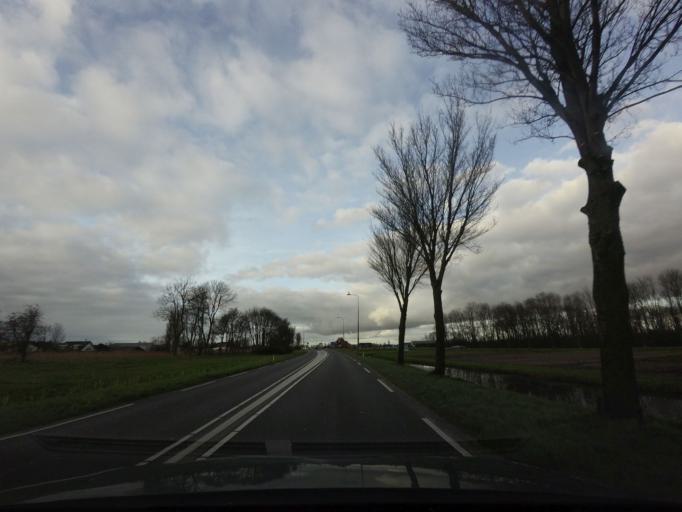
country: NL
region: North Holland
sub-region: Gemeente Langedijk
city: Broek op Langedijk
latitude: 52.7060
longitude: 4.8233
